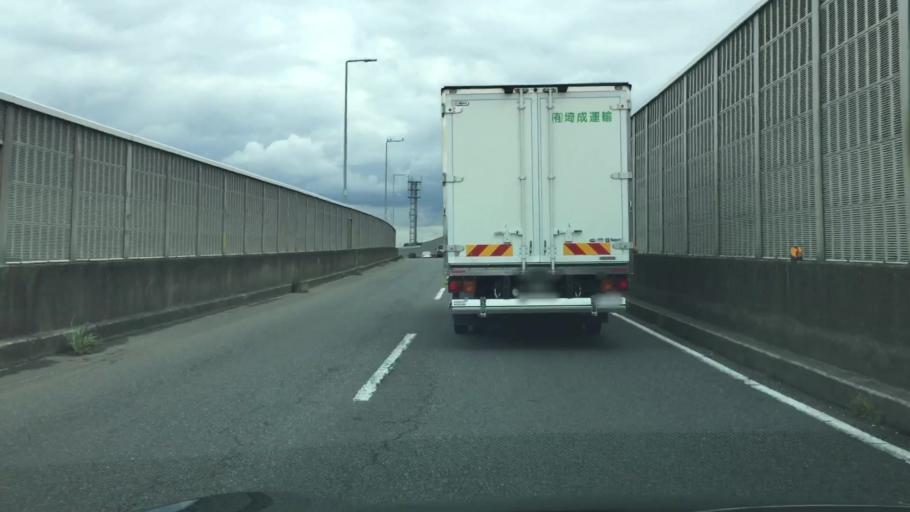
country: JP
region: Saitama
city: Kamifukuoka
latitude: 35.9190
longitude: 139.5574
